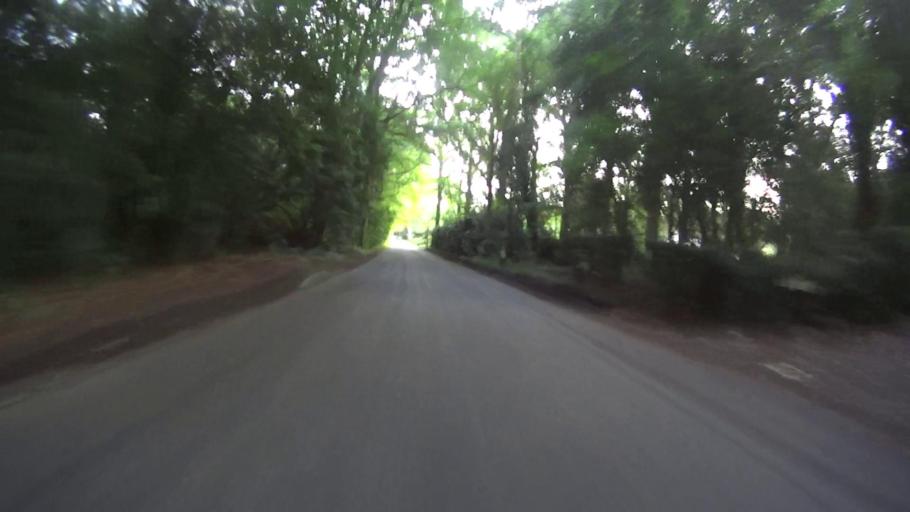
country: GB
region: England
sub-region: West Sussex
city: Maidenbower
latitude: 51.1173
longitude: -0.1319
